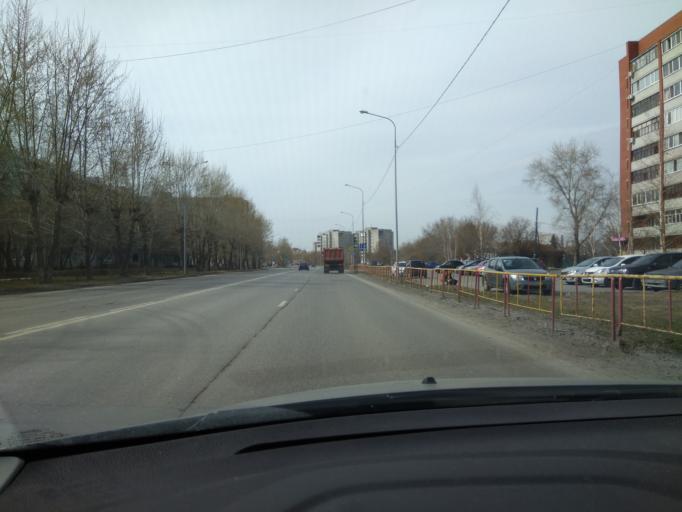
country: RU
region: Tjumen
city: Melioratorov
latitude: 57.1863
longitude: 65.5871
